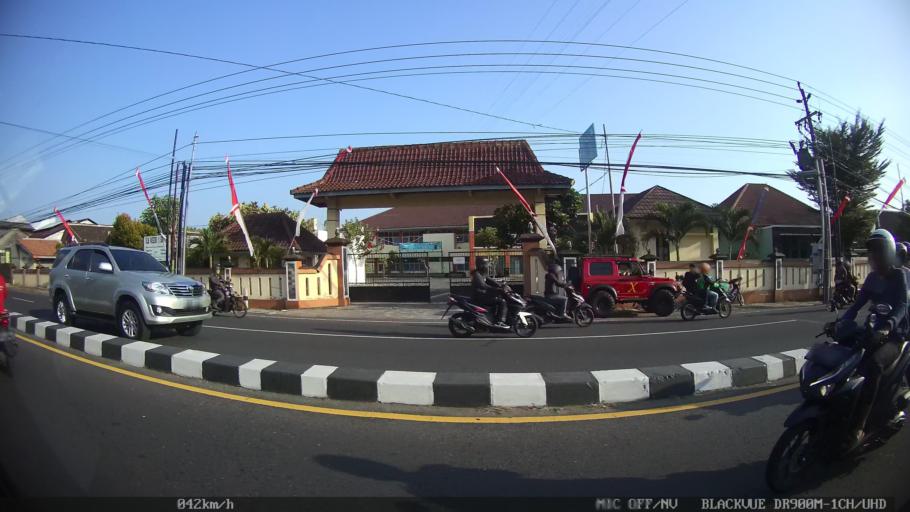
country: ID
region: Daerah Istimewa Yogyakarta
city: Gamping Lor
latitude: -7.8002
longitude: 110.3385
